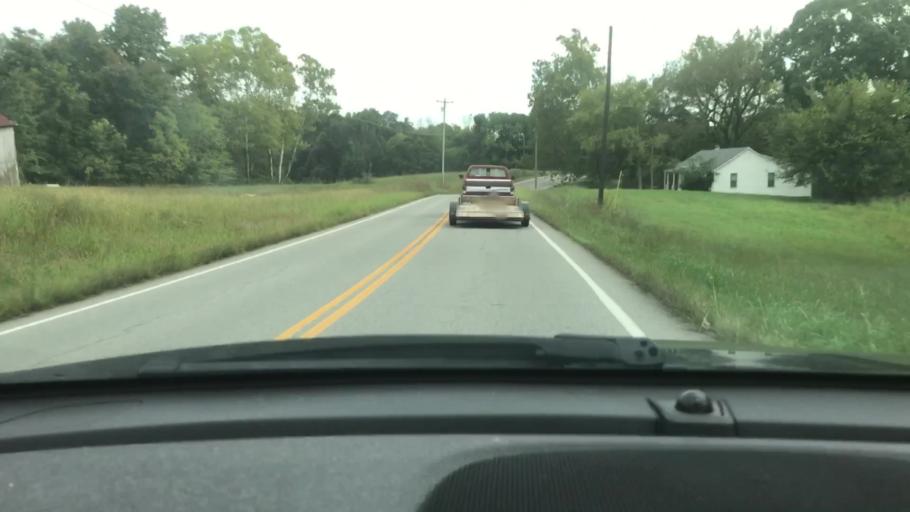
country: US
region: Tennessee
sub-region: Dickson County
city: Charlotte
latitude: 36.2620
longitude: -87.2204
